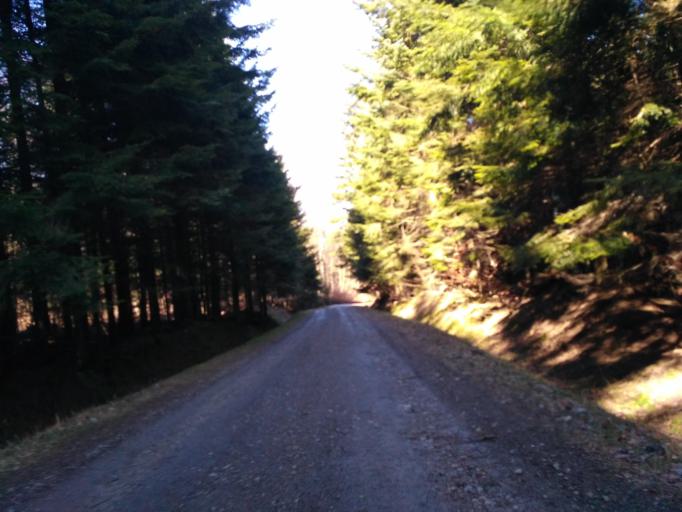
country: PL
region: Subcarpathian Voivodeship
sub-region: Powiat strzyzowski
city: Babica
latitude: 49.9534
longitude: 21.8679
